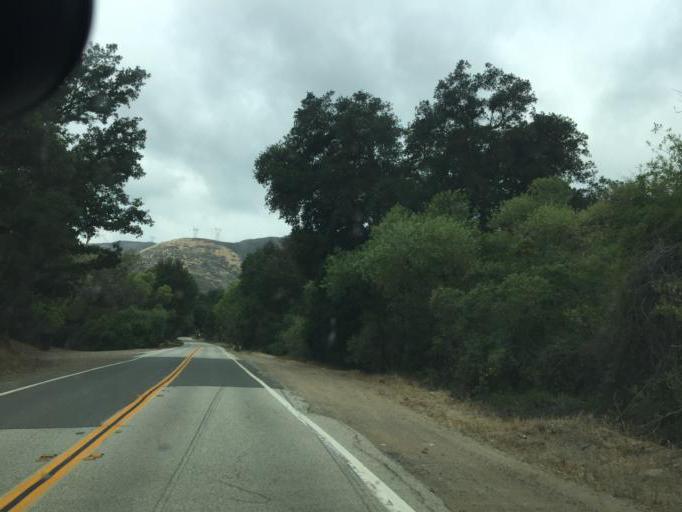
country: US
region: California
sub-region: Los Angeles County
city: Green Valley
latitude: 34.5537
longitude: -118.4138
